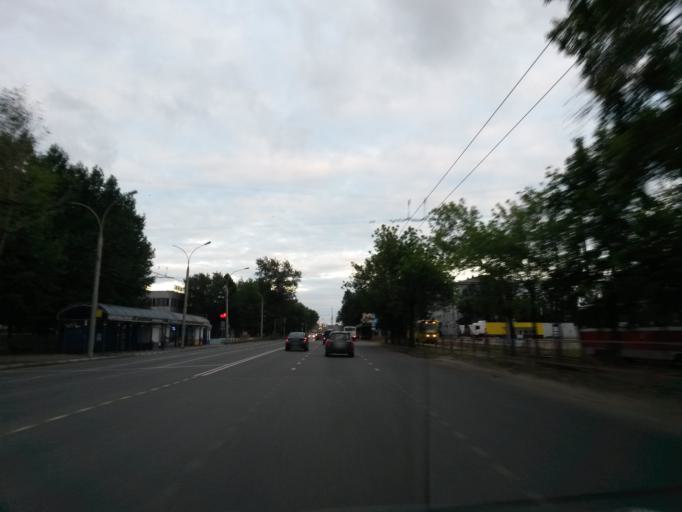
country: RU
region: Jaroslavl
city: Yaroslavl
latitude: 57.6480
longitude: 39.8498
